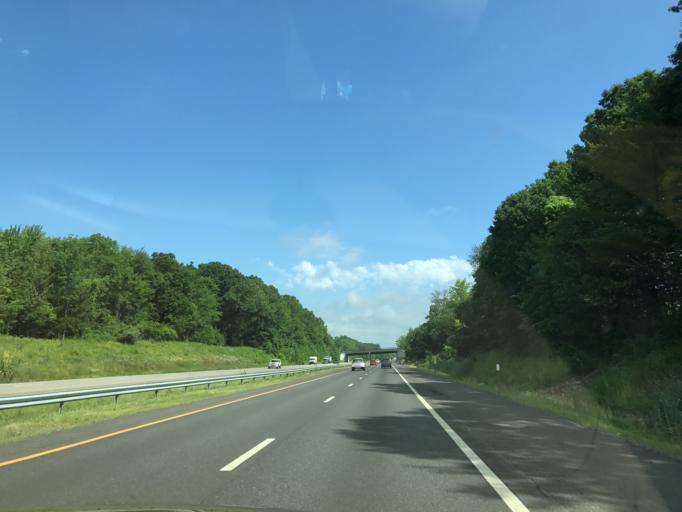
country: US
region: New York
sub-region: Orange County
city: Orange Lake
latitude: 41.5593
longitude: -74.0813
